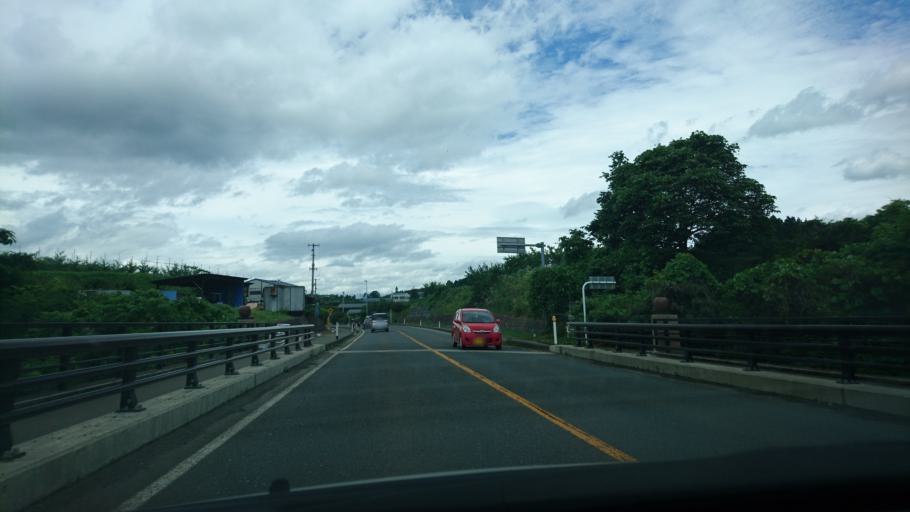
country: JP
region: Iwate
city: Morioka-shi
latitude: 39.6097
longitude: 141.2029
